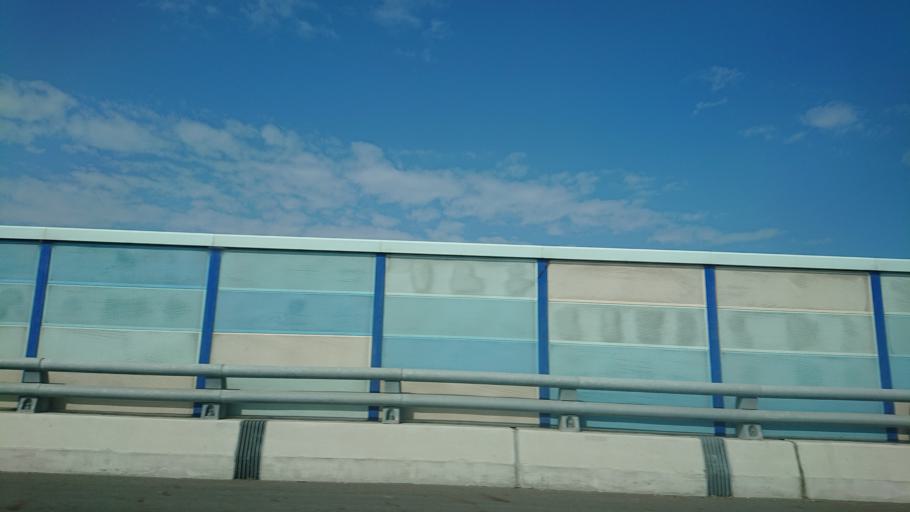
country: TW
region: Taiwan
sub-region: Changhua
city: Chang-hua
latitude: 23.9600
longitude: 120.3353
